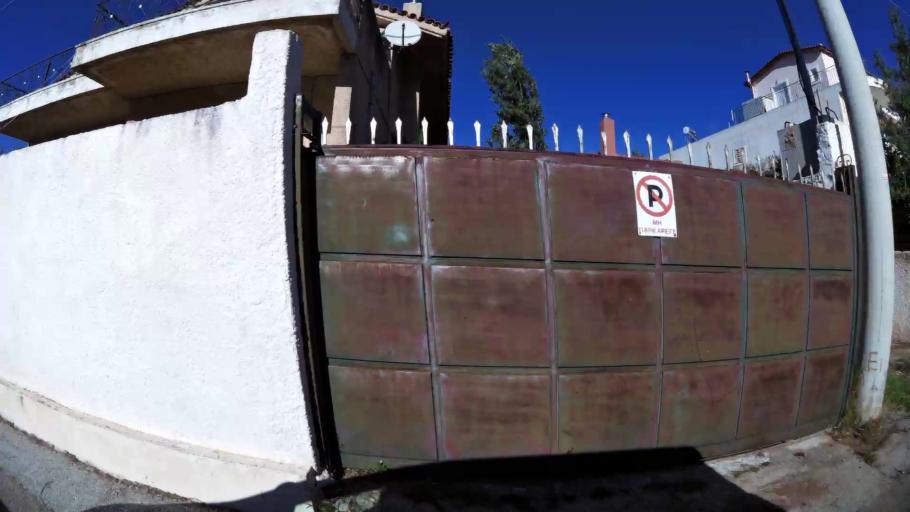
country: GR
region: Attica
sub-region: Nomarchia Anatolikis Attikis
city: Kalyvia Thorikou
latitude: 37.8337
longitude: 23.9258
